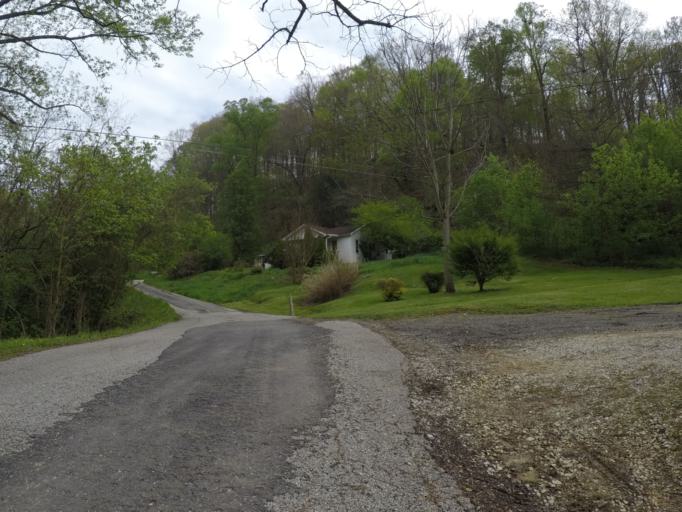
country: US
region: West Virginia
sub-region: Cabell County
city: Huntington
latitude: 38.3920
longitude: -82.4841
